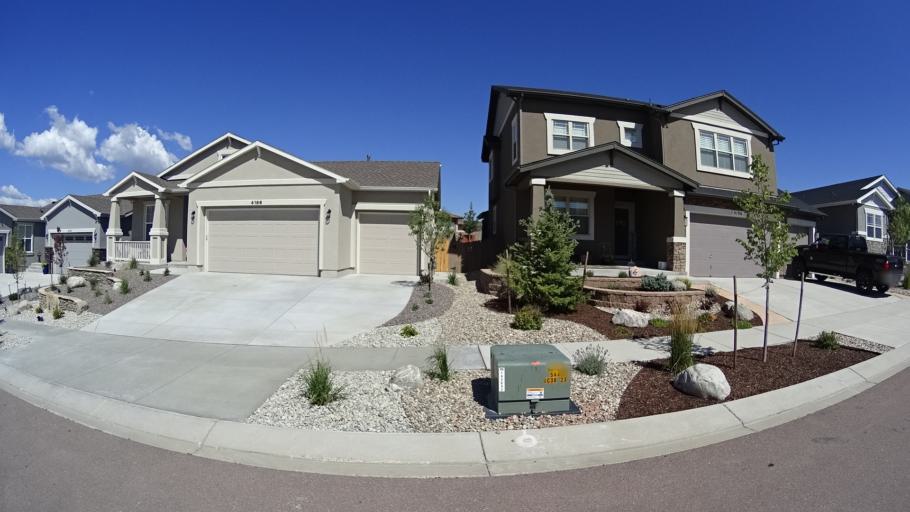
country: US
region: Colorado
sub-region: El Paso County
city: Black Forest
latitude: 38.9799
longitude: -104.7472
